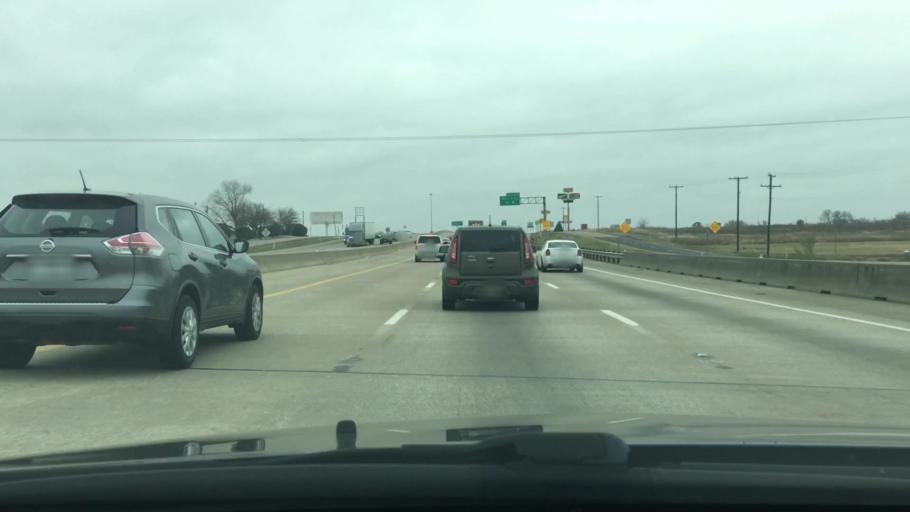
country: US
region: Texas
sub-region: Dallas County
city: Wilmer
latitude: 32.5969
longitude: -96.6822
